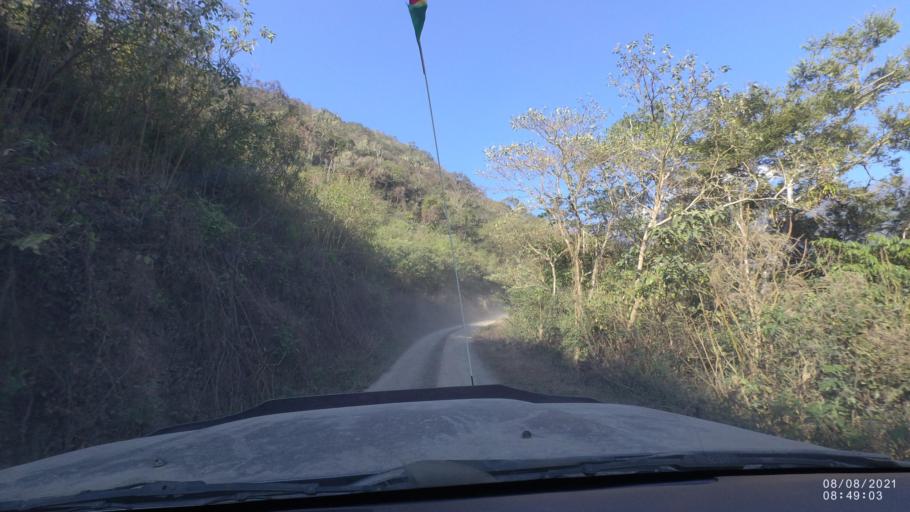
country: BO
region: La Paz
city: Quime
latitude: -16.5319
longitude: -66.7562
